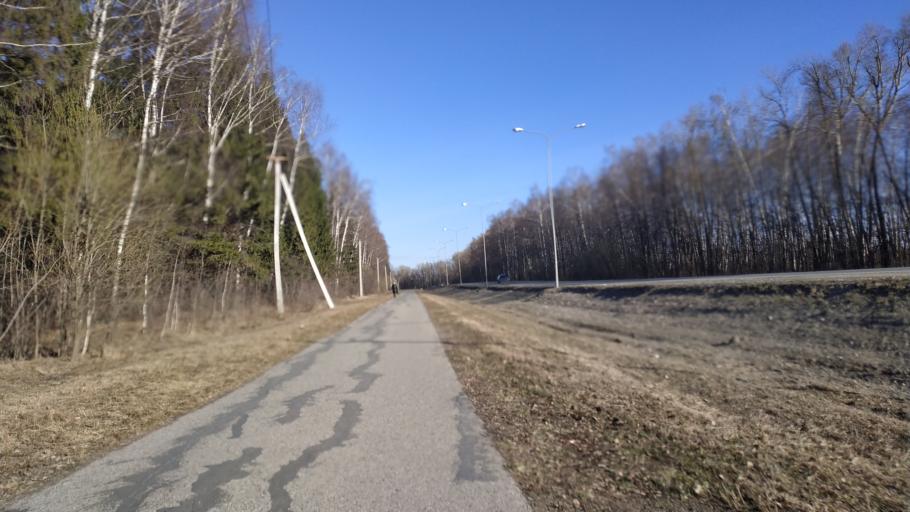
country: RU
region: Chuvashia
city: Novyye Lapsary
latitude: 56.1310
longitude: 47.1137
